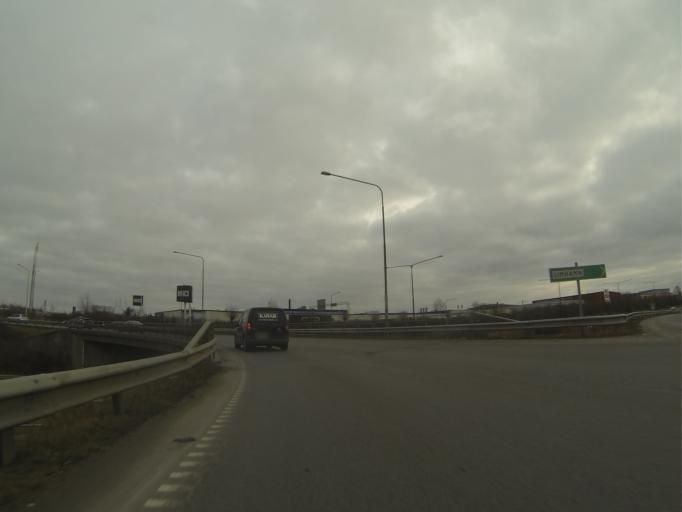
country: SE
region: Skane
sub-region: Malmo
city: Malmoe
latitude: 55.5696
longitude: 13.0444
